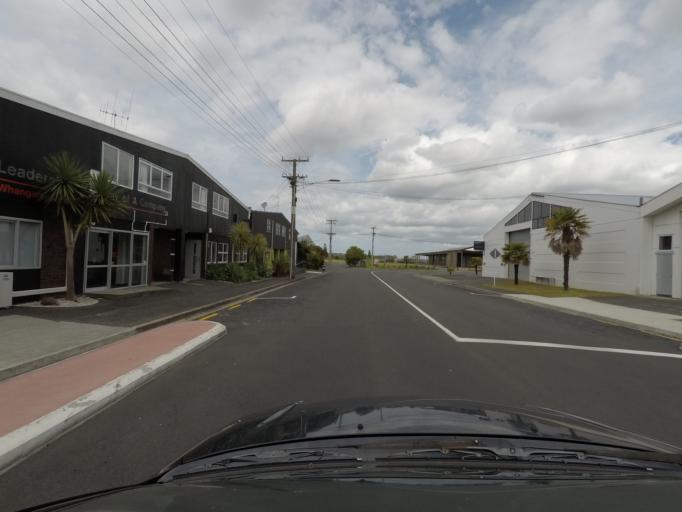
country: NZ
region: Northland
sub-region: Whangarei
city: Whangarei
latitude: -35.7280
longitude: 174.3305
